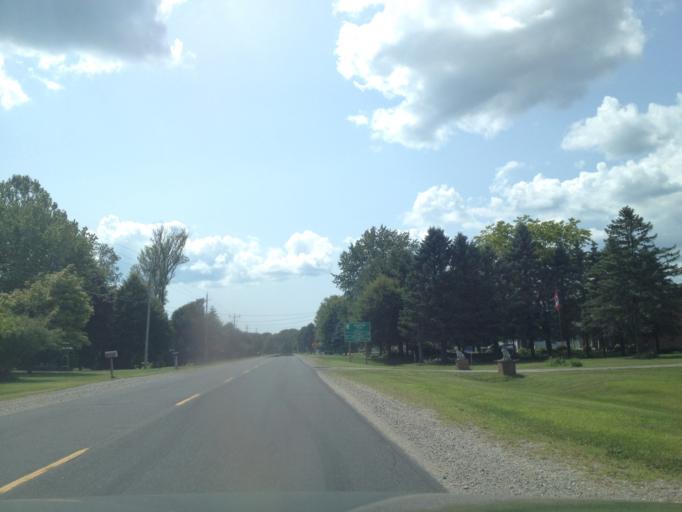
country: CA
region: Ontario
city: Aylmer
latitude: 42.6759
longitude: -80.9807
